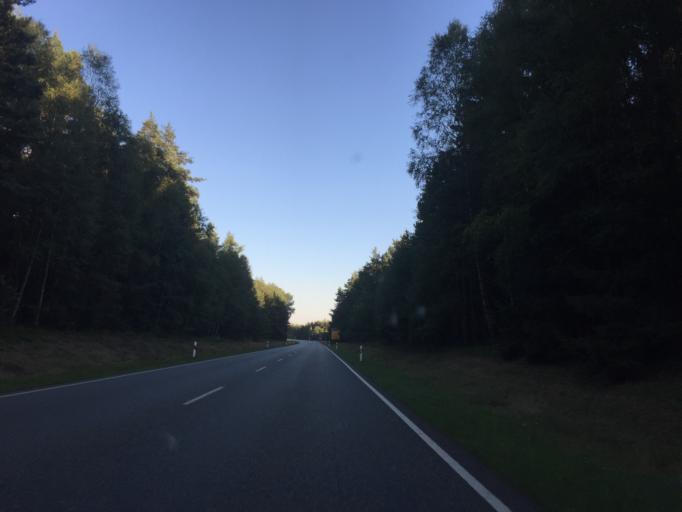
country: DE
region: Bavaria
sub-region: Upper Palatinate
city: Schwarzenbach
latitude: 49.7283
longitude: 11.9630
